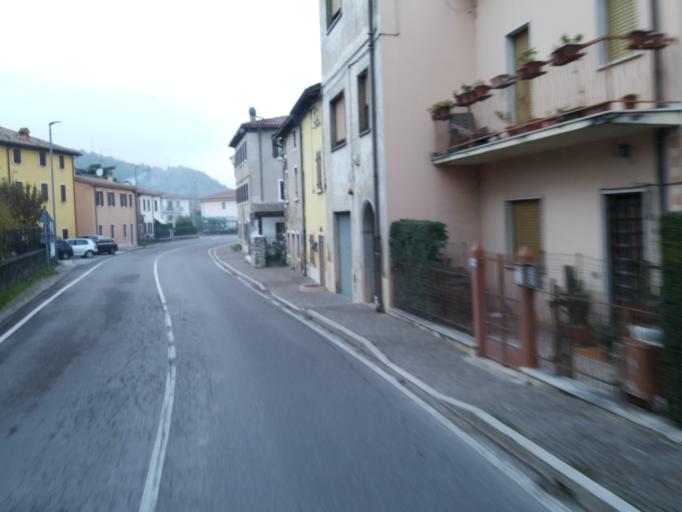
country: IT
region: Veneto
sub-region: Provincia di Verona
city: Pastrengo
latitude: 45.5177
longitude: 10.8022
